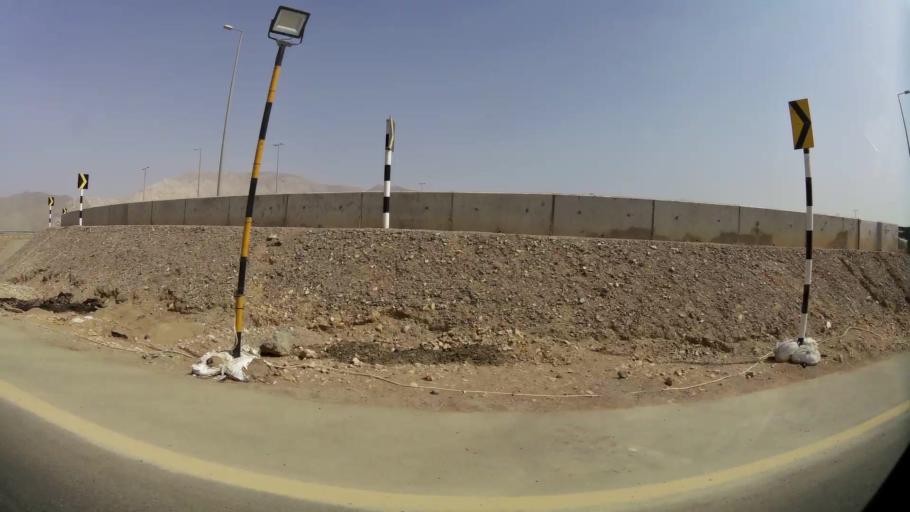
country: OM
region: Muhafazat Masqat
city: Bawshar
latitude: 23.5708
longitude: 58.4067
